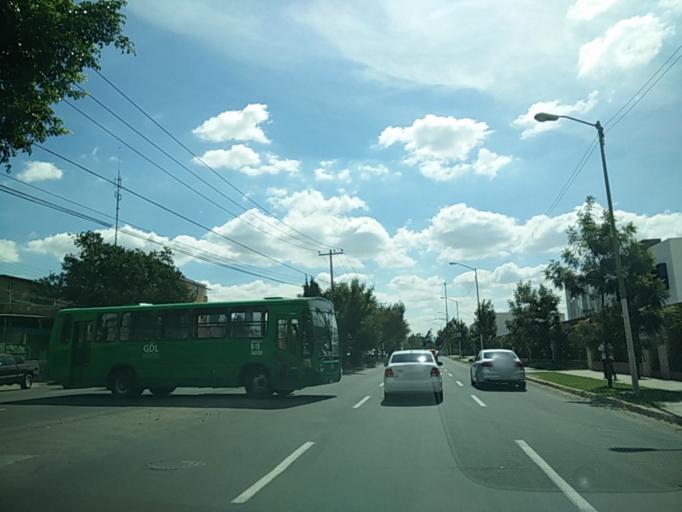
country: MX
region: Jalisco
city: Nuevo Mexico
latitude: 20.7284
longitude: -103.4311
